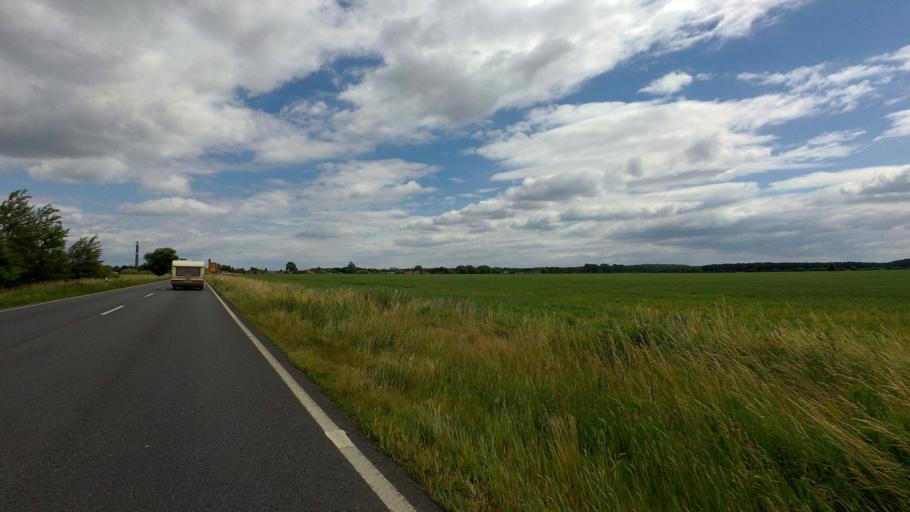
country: DE
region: Brandenburg
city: Grossraschen
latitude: 51.5864
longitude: 13.9485
